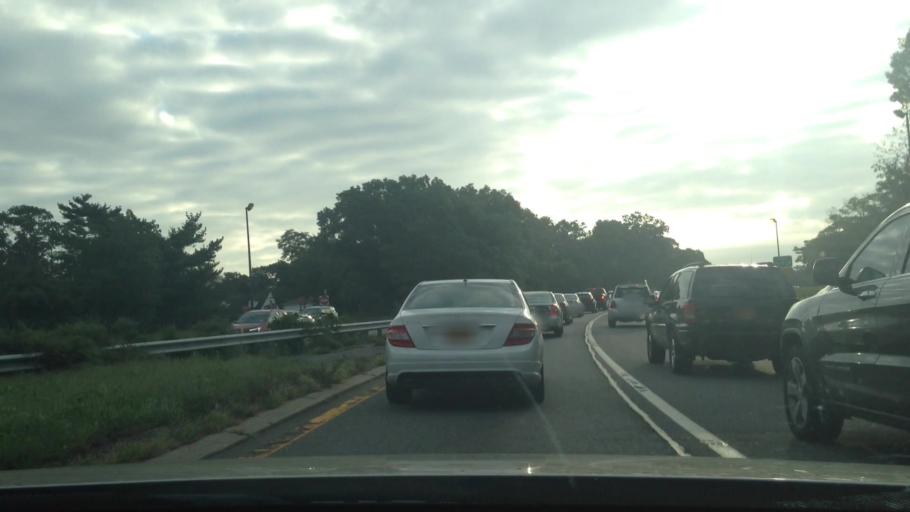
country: US
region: New York
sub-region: Nassau County
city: South Hempstead
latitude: 40.6900
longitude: -73.6322
